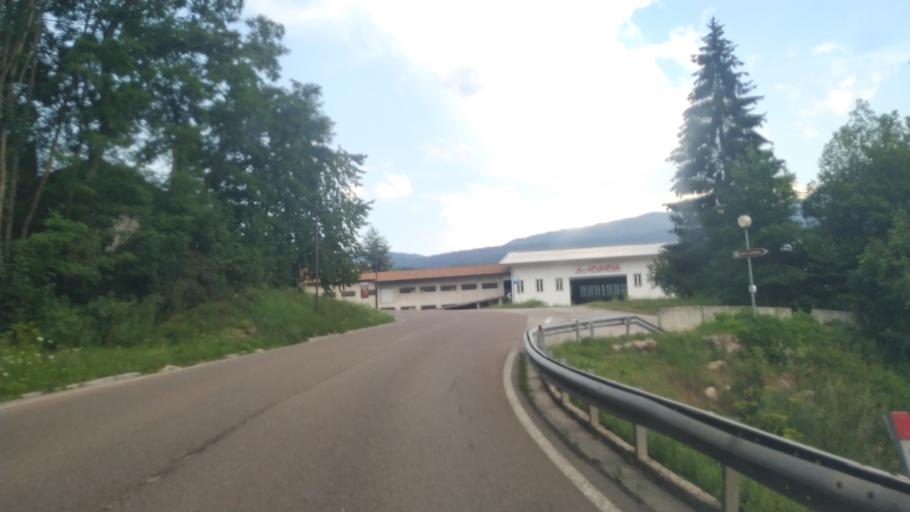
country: IT
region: Trentino-Alto Adige
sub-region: Provincia di Trento
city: Cavareno
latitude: 46.4029
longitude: 11.1308
